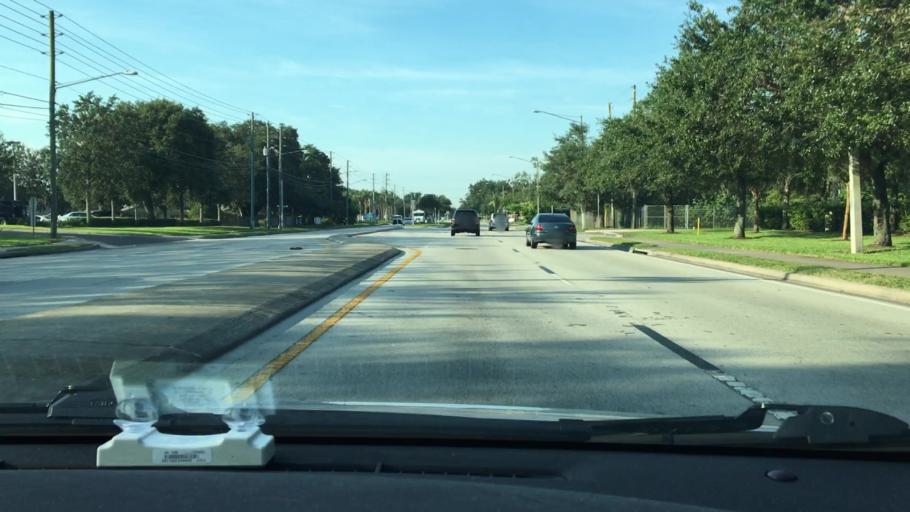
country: US
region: Florida
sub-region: Seminole County
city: Goldenrod
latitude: 28.5947
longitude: -81.2865
